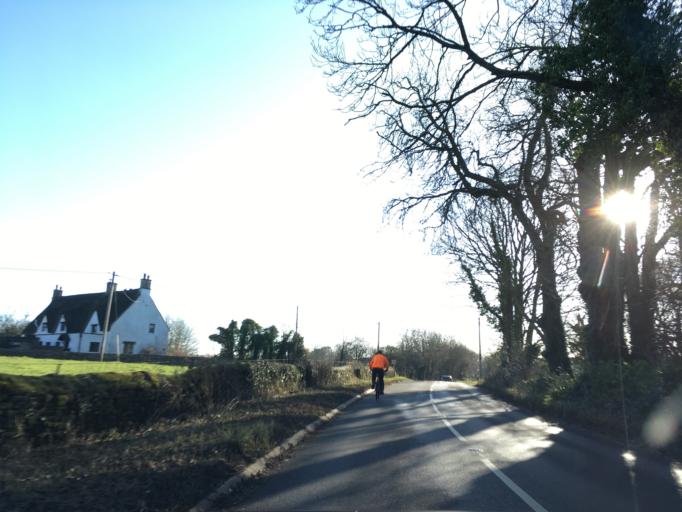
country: GB
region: England
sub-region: Wiltshire
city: Nettleton
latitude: 51.4979
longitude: -2.2218
